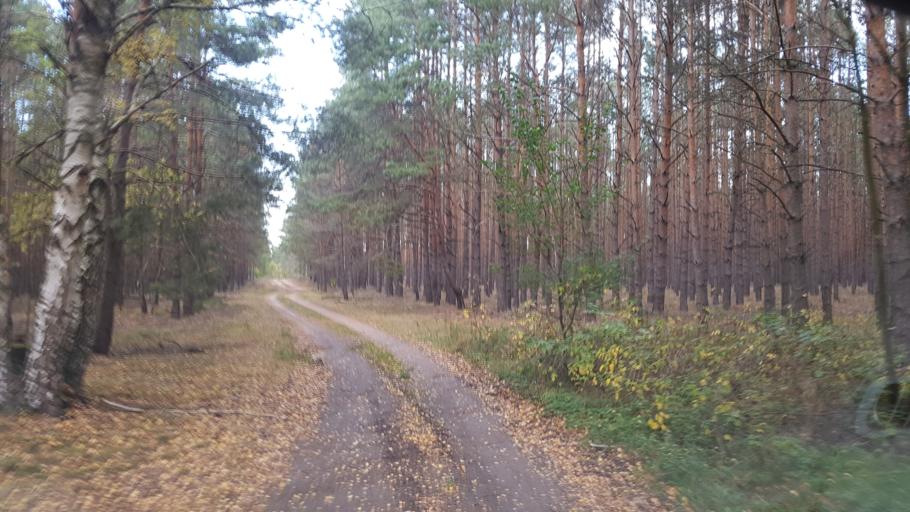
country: DE
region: Brandenburg
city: Schonborn
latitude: 51.6526
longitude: 13.5081
